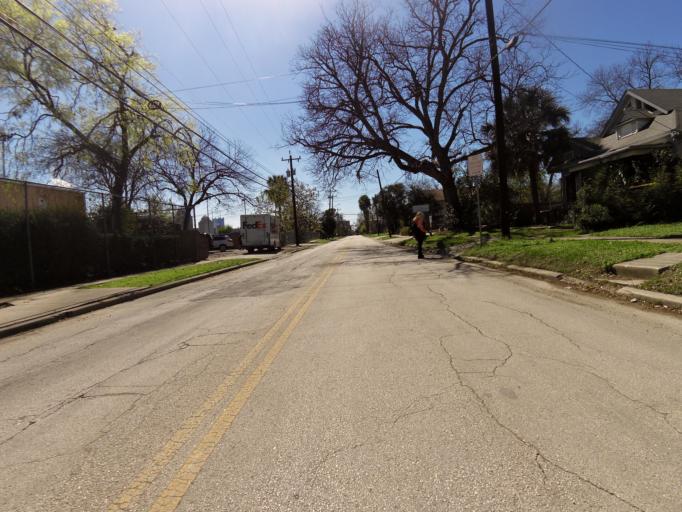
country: US
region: Texas
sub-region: Bexar County
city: San Antonio
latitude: 29.4379
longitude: -98.4865
